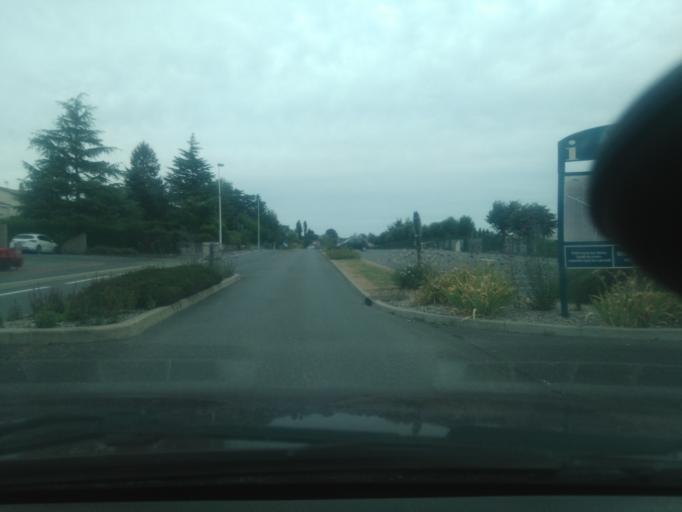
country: FR
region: Pays de la Loire
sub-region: Departement de la Vendee
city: La Chataigneraie
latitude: 46.6532
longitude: -0.7487
